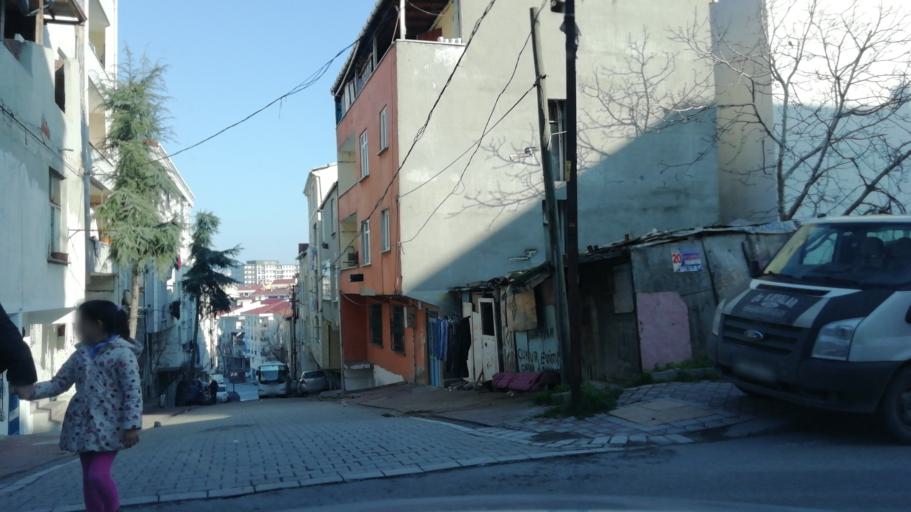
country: TR
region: Istanbul
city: Esenyurt
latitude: 41.0276
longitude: 28.6905
